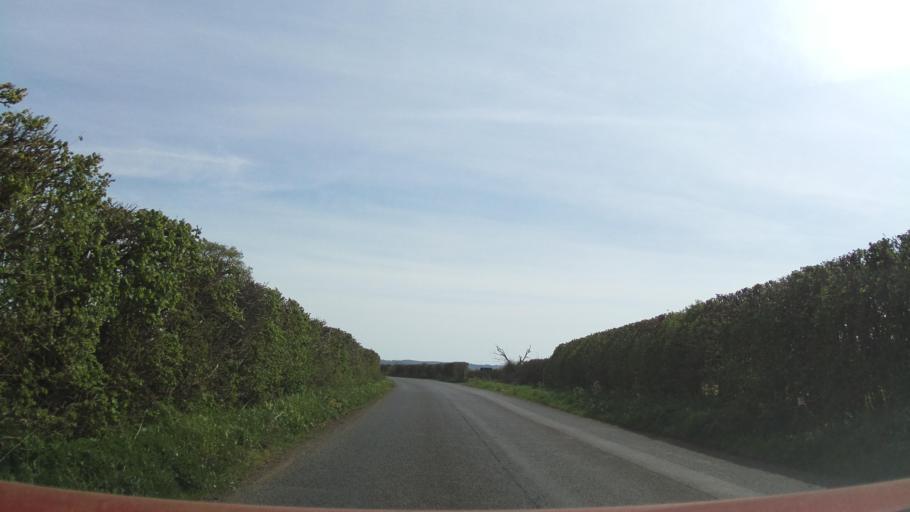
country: GB
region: England
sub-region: Somerset
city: Ilchester
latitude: 51.0227
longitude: -2.6439
